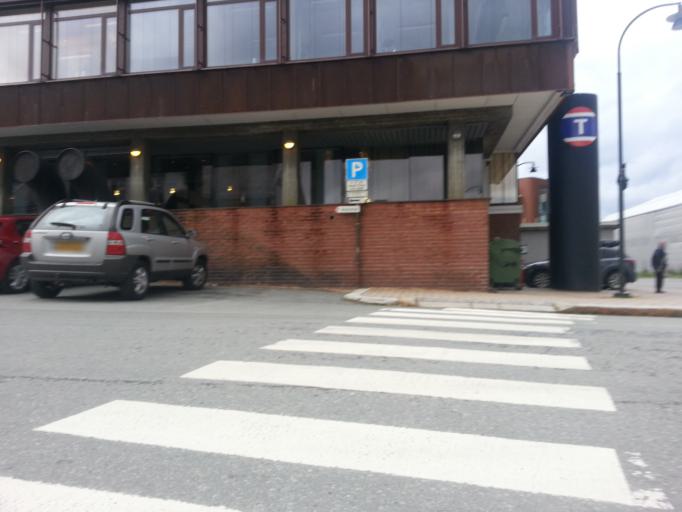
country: NO
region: Troms
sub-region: Tromso
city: Tromso
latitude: 69.6481
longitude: 18.9608
